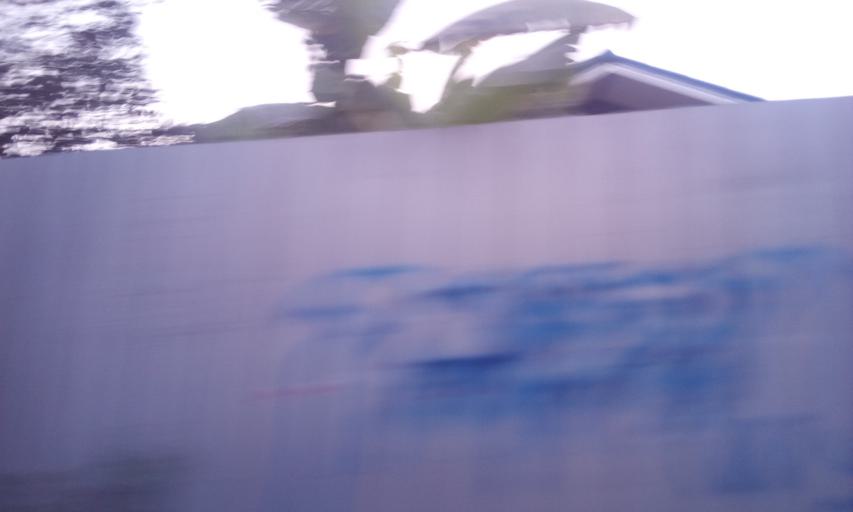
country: TH
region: Bangkok
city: Nong Chok
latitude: 13.8503
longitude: 100.8852
